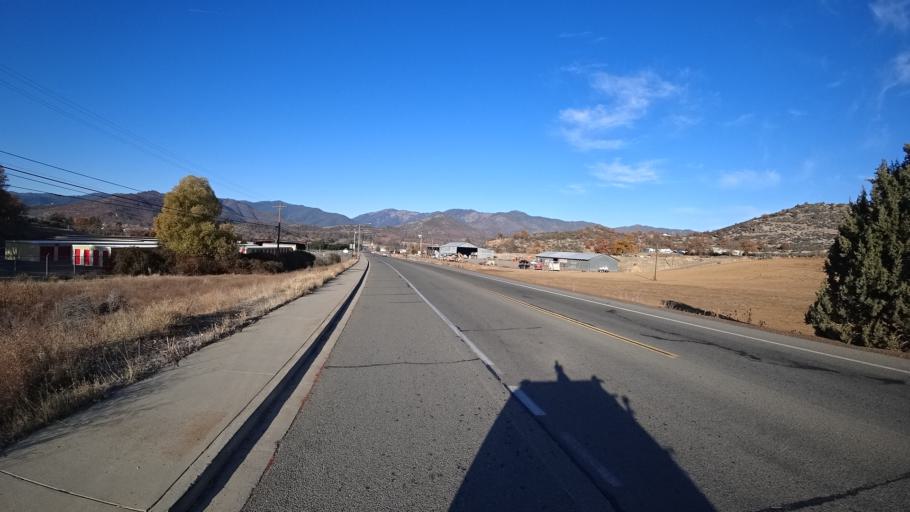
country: US
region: California
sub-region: Siskiyou County
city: Yreka
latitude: 41.7149
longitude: -122.6289
